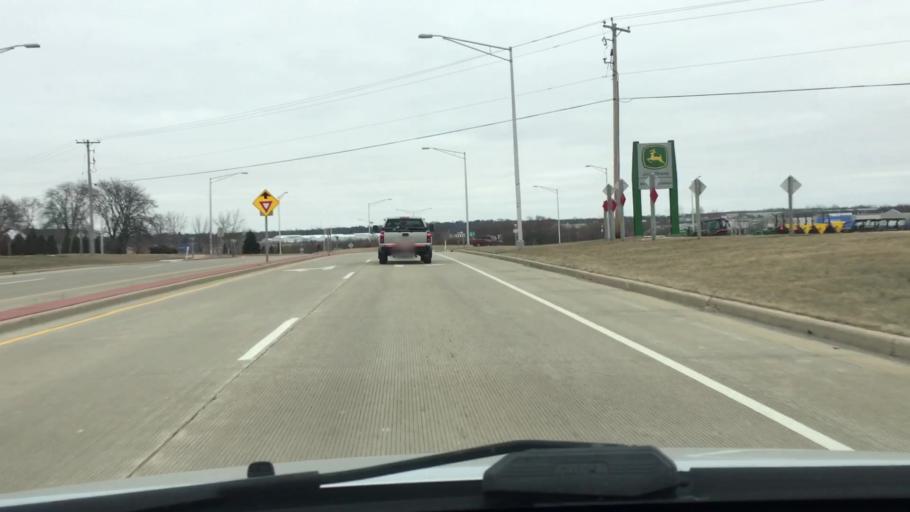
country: US
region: Wisconsin
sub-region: Jefferson County
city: Watertown
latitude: 43.1600
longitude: -88.7362
